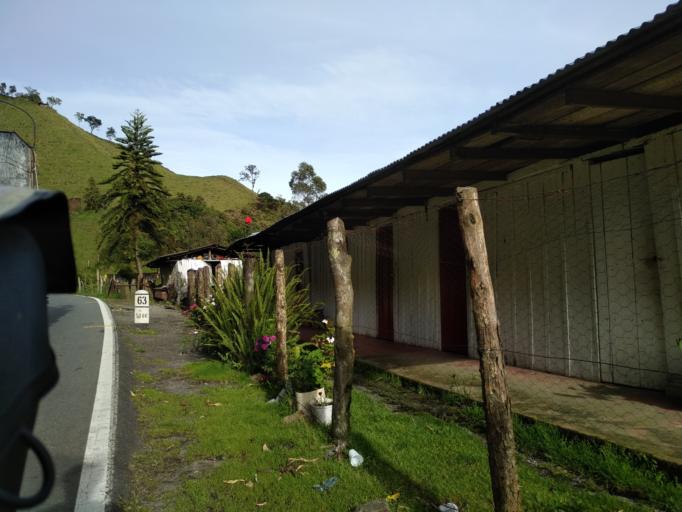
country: CO
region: Tolima
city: Herveo
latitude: 5.1392
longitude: -75.1624
